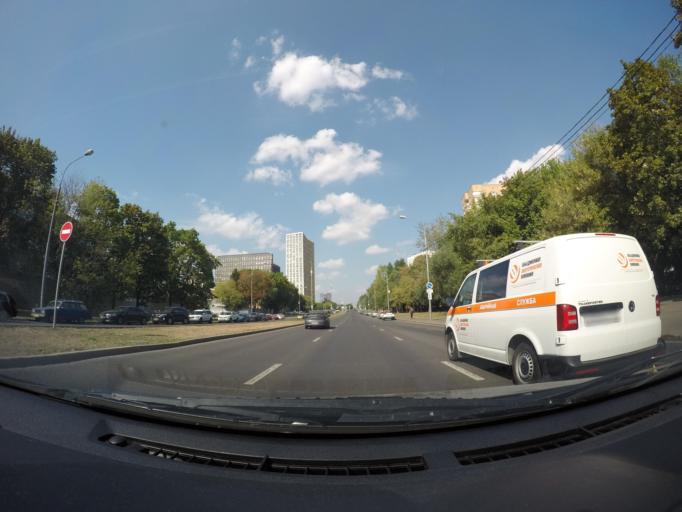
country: RU
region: Moskovskaya
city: Levoberezhnyy
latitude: 55.8641
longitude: 37.4857
